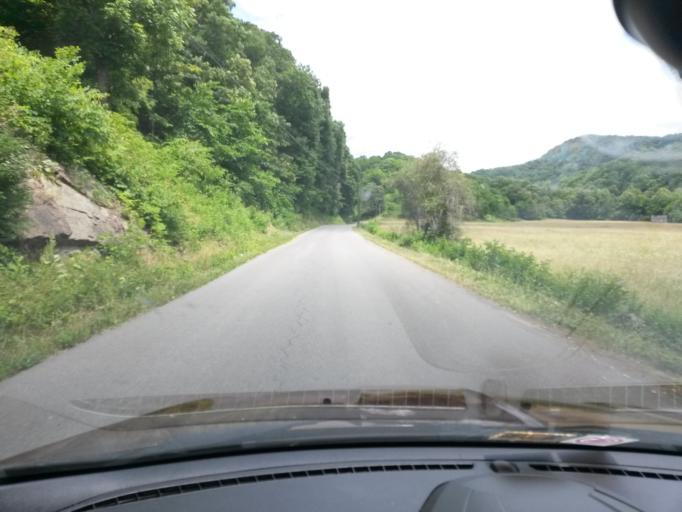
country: US
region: West Virginia
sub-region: Monroe County
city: Union
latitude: 37.5090
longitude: -80.5734
